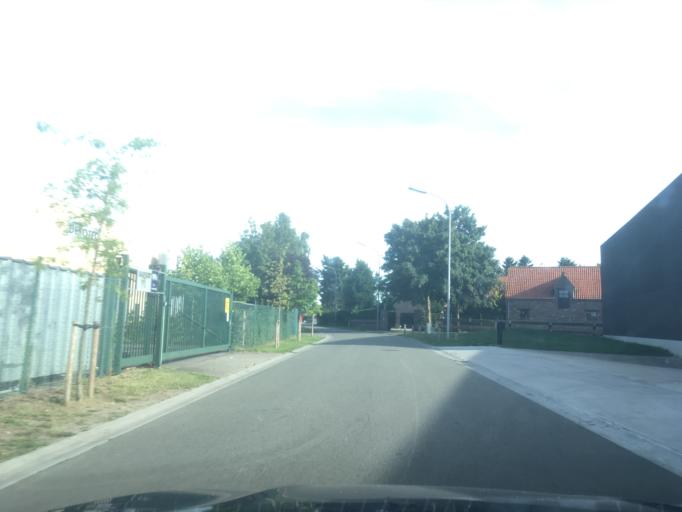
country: BE
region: Flanders
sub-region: Provincie West-Vlaanderen
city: Izegem
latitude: 50.9260
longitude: 3.1822
